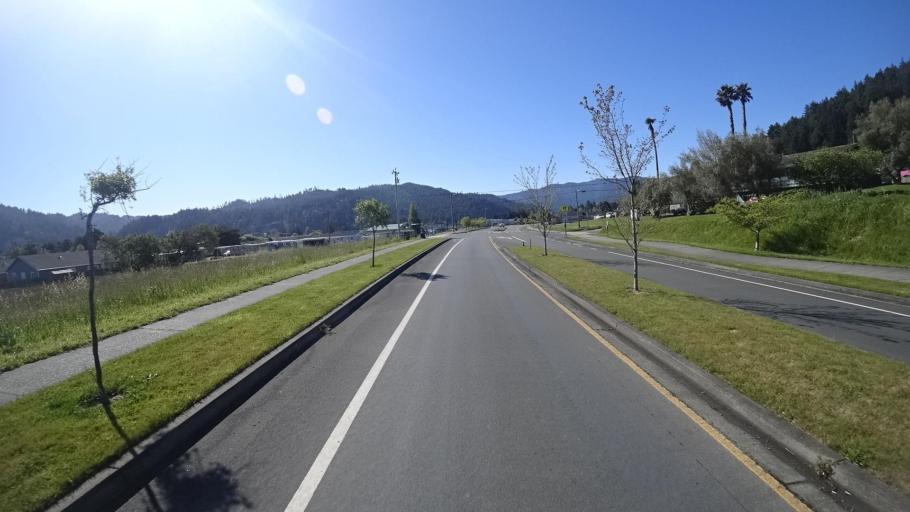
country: US
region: California
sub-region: Humboldt County
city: Rio Dell
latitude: 40.5031
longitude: -124.1073
